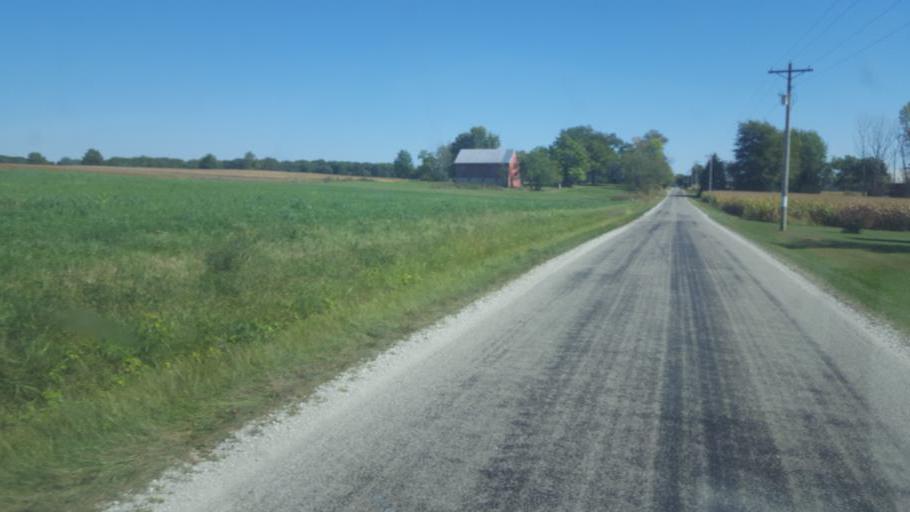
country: US
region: Ohio
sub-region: Huron County
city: Willard
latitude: 40.9458
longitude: -82.8253
